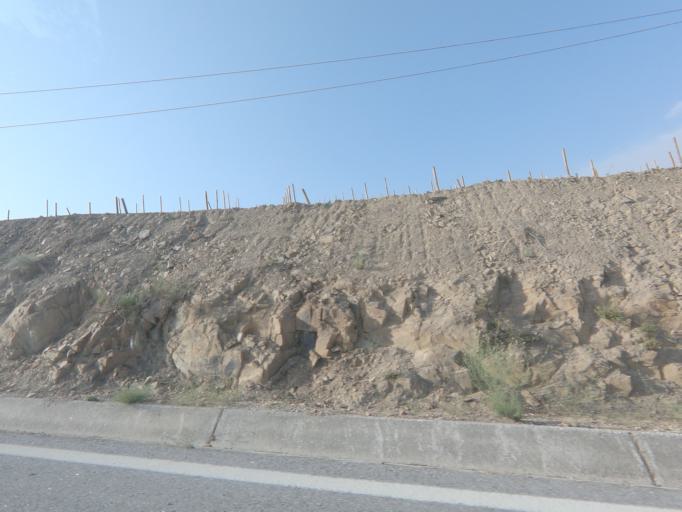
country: PT
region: Viseu
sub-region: Tabuaco
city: Tabuaco
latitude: 41.1399
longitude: -7.5446
